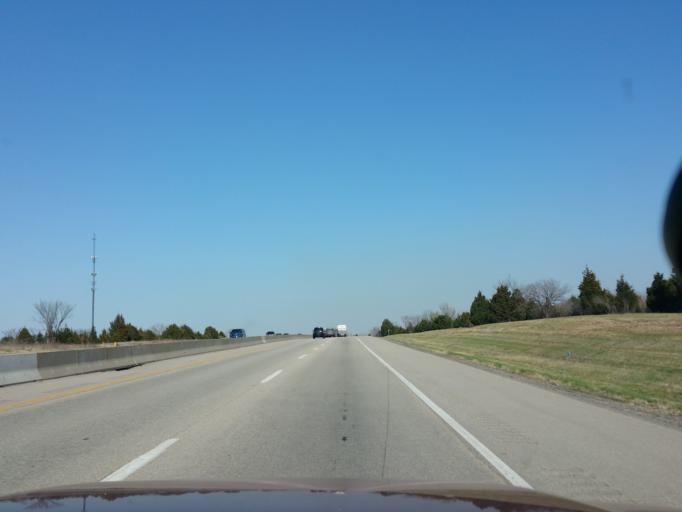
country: US
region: Kansas
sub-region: Douglas County
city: Lawrence
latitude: 39.0093
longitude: -95.1565
